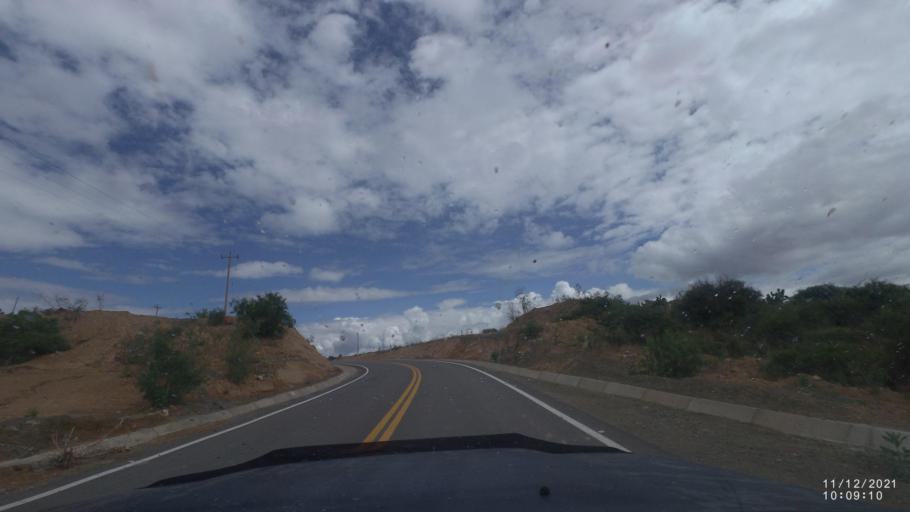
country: BO
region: Cochabamba
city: Tarata
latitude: -17.6589
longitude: -65.9683
